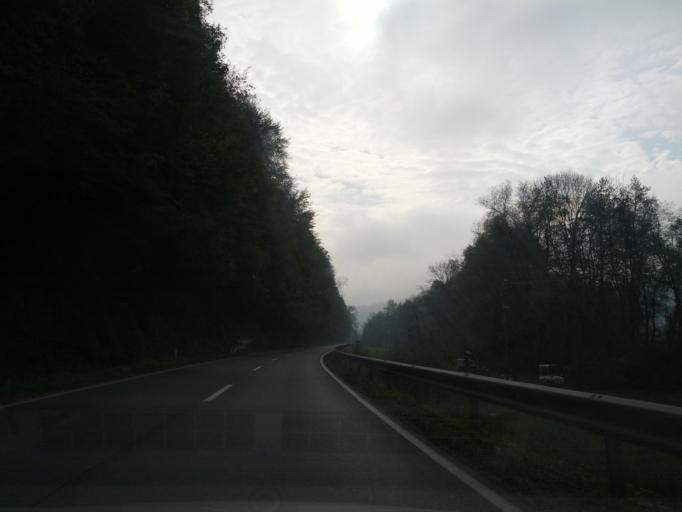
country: SI
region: Litija
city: Litija
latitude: 46.1009
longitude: 14.7995
